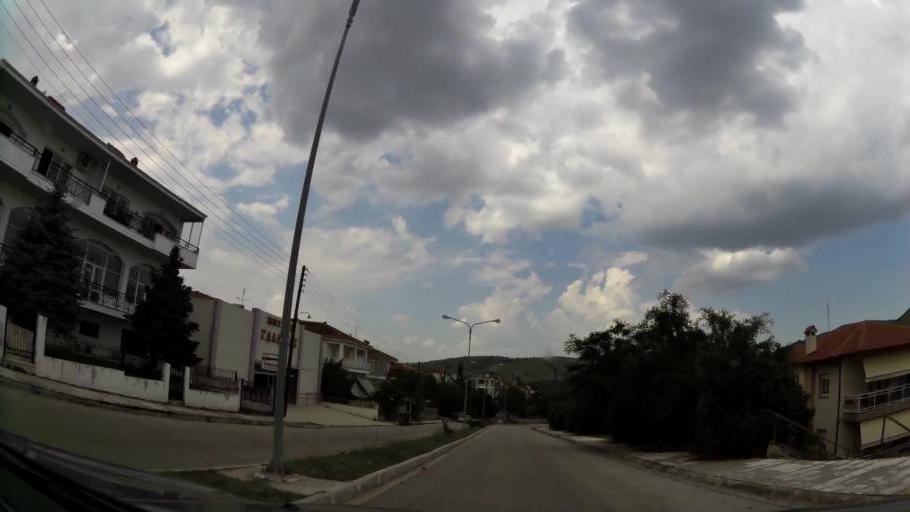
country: GR
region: West Macedonia
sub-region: Nomos Kozanis
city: Koila
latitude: 40.3264
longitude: 21.8238
